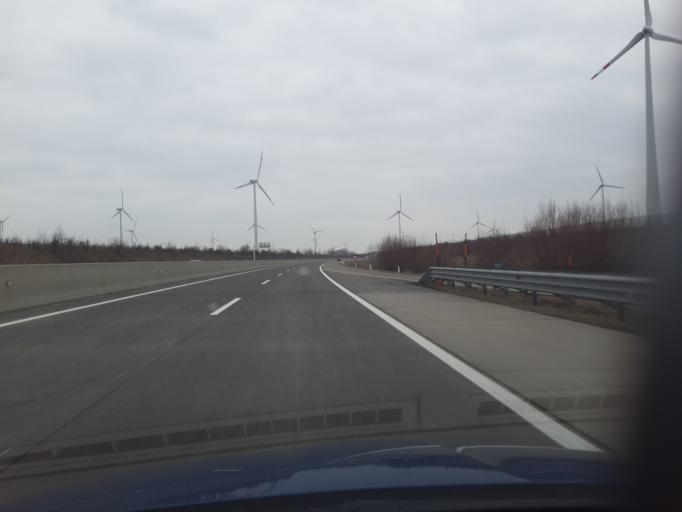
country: AT
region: Burgenland
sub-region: Politischer Bezirk Neusiedl am See
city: Potzneusiedl
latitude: 48.0259
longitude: 16.9345
